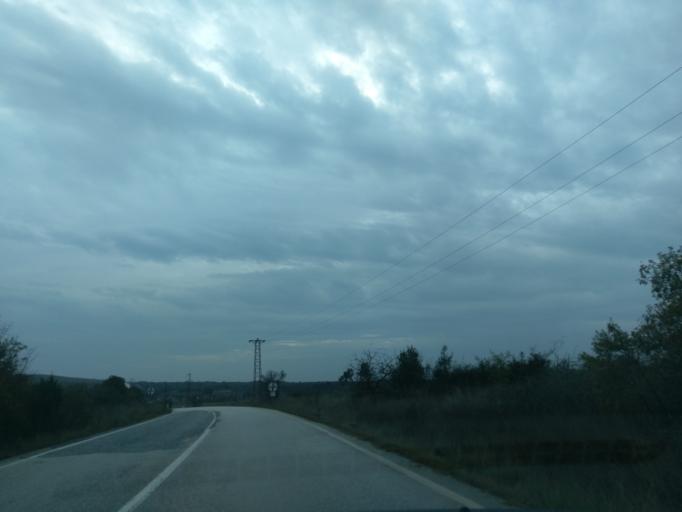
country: TR
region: Istanbul
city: Canta
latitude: 41.1737
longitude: 28.0915
